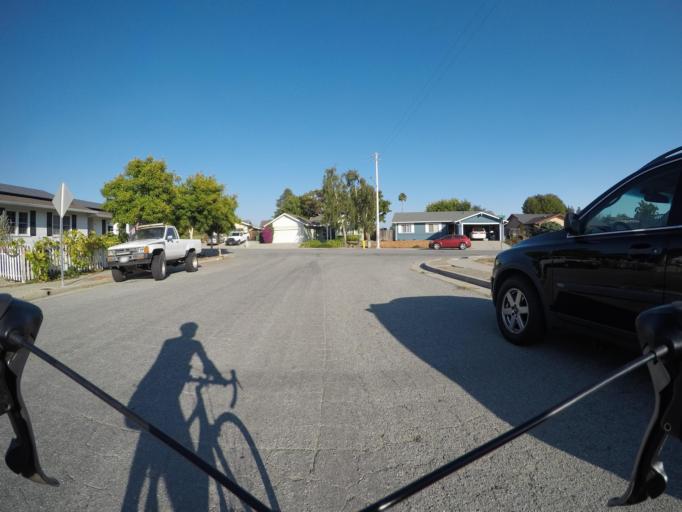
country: US
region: California
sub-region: Santa Cruz County
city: Live Oak
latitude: 37.0058
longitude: -121.9771
